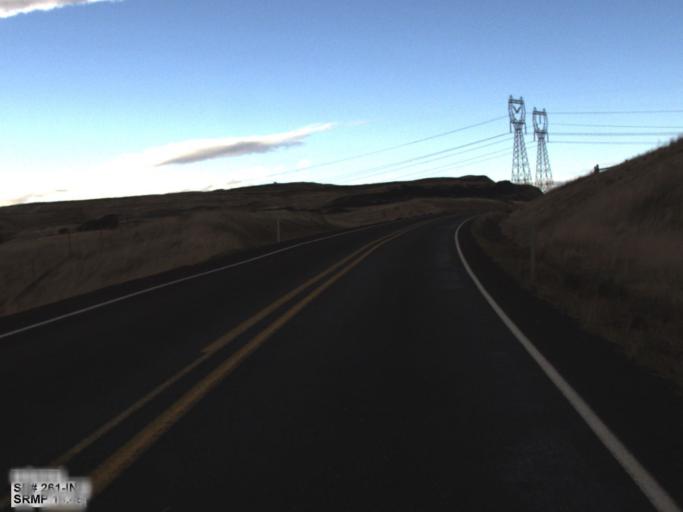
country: US
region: Washington
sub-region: Walla Walla County
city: Waitsburg
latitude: 46.5715
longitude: -118.2023
